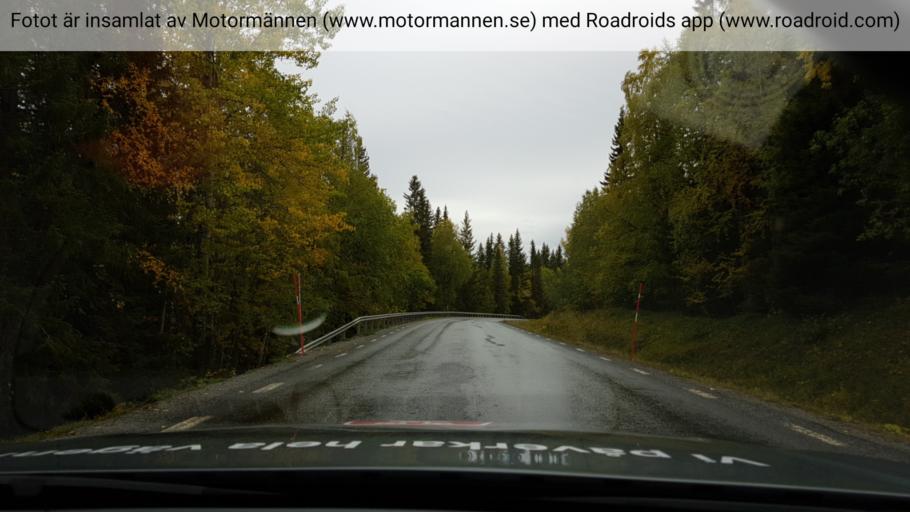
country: SE
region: Vaesterbotten
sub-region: Vilhelmina Kommun
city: Sjoberg
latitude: 64.6586
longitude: 16.3147
